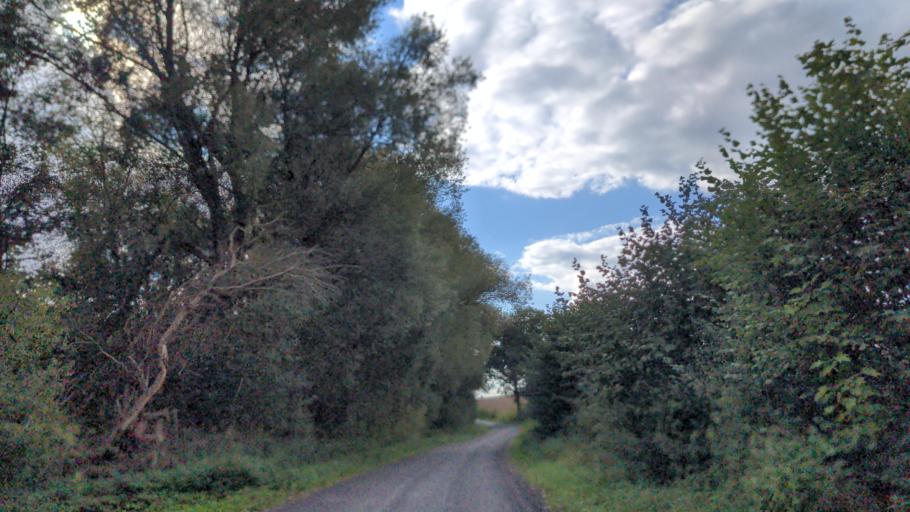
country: DE
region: Schleswig-Holstein
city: Stockelsdorf
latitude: 53.9281
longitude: 10.6279
